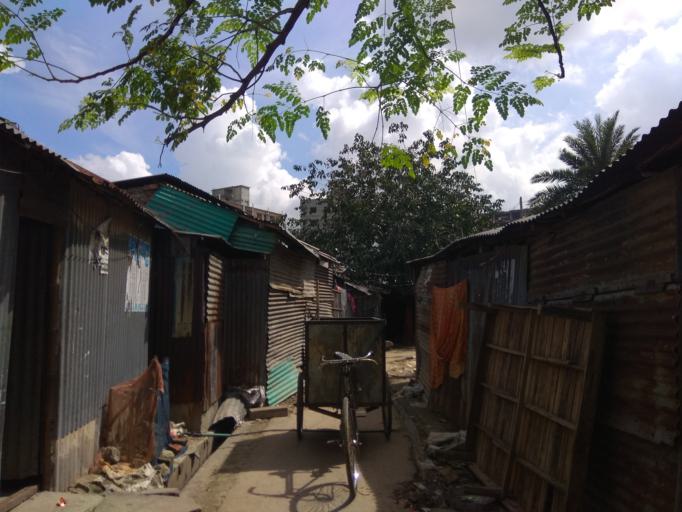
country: BD
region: Dhaka
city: Paltan
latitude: 23.8107
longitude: 90.3875
